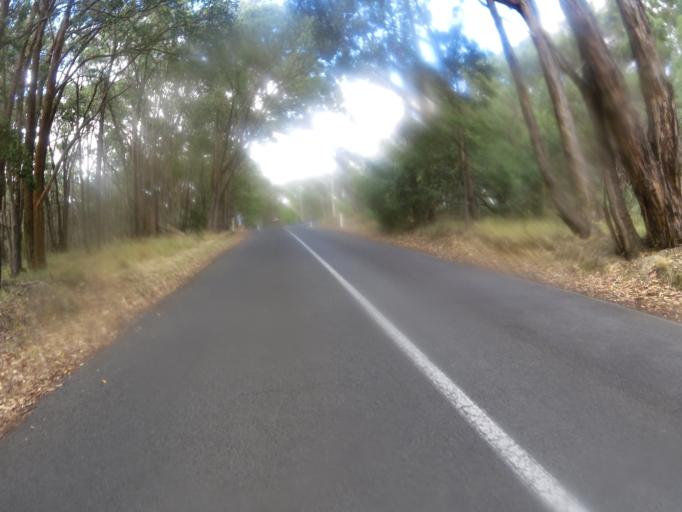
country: AU
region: Victoria
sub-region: Ballarat North
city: Mount Clear
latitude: -37.6350
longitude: 143.8960
